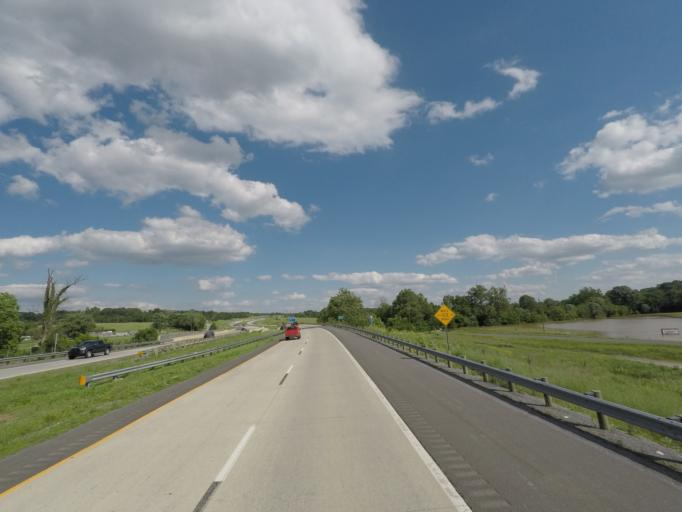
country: US
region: West Virginia
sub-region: Berkeley County
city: Martinsburg
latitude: 39.4256
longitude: -77.9396
